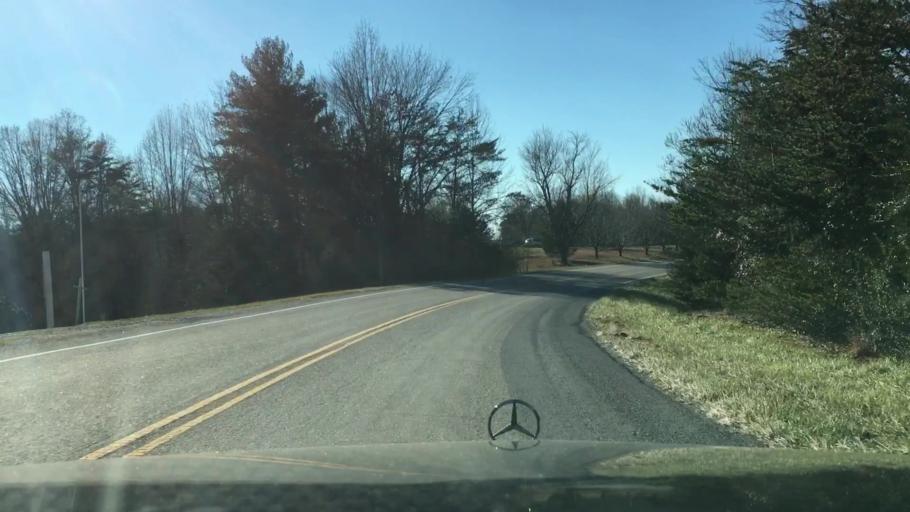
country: US
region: Virginia
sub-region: City of Bedford
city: Bedford
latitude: 37.2265
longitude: -79.5411
